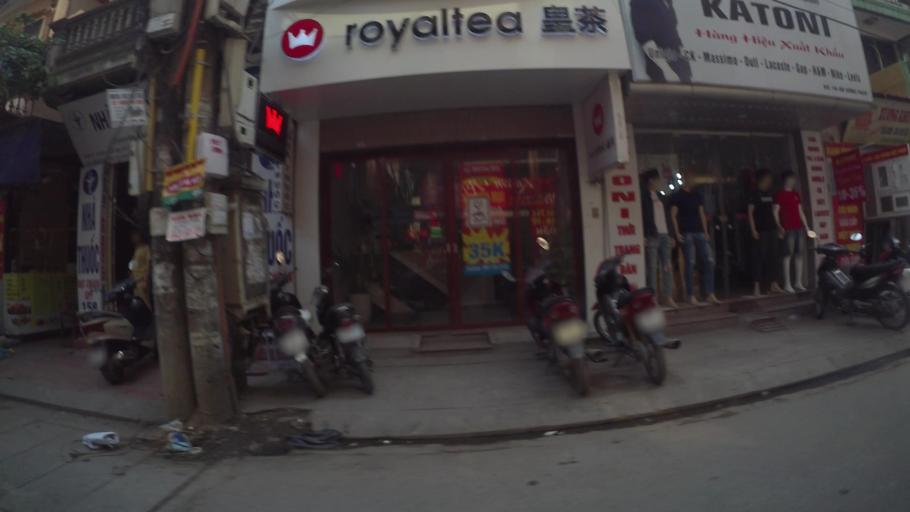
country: VN
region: Ha Noi
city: Thanh Xuan
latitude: 20.9890
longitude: 105.8180
